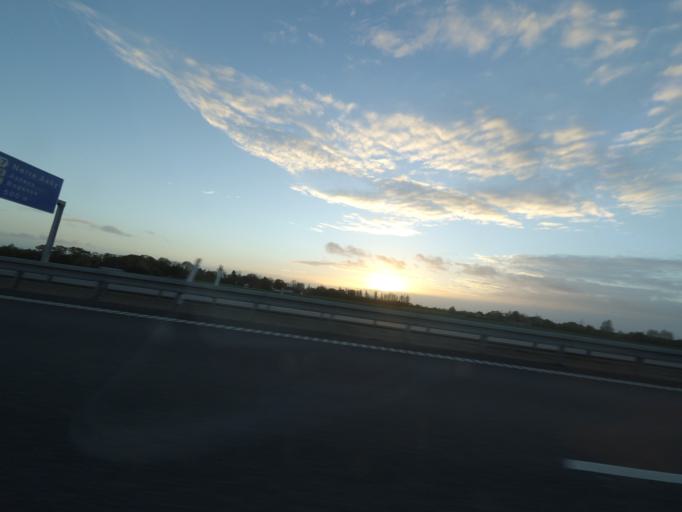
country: DK
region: South Denmark
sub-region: Middelfart Kommune
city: Norre Aby
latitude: 55.4761
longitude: 9.8869
